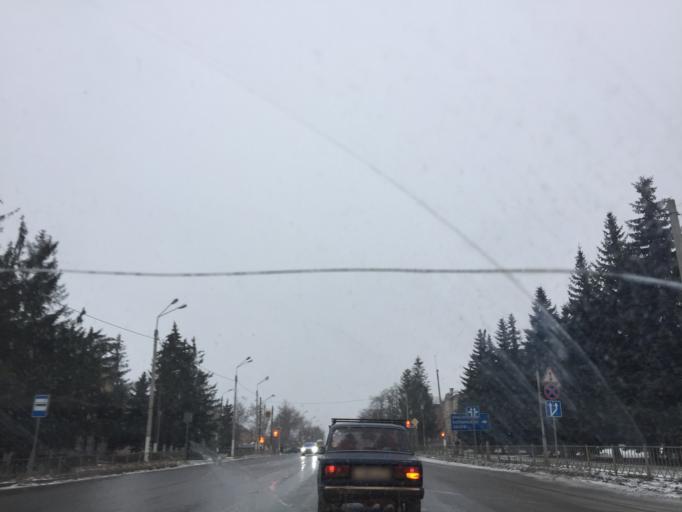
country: RU
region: Tula
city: Plavsk
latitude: 53.7070
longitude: 37.2930
